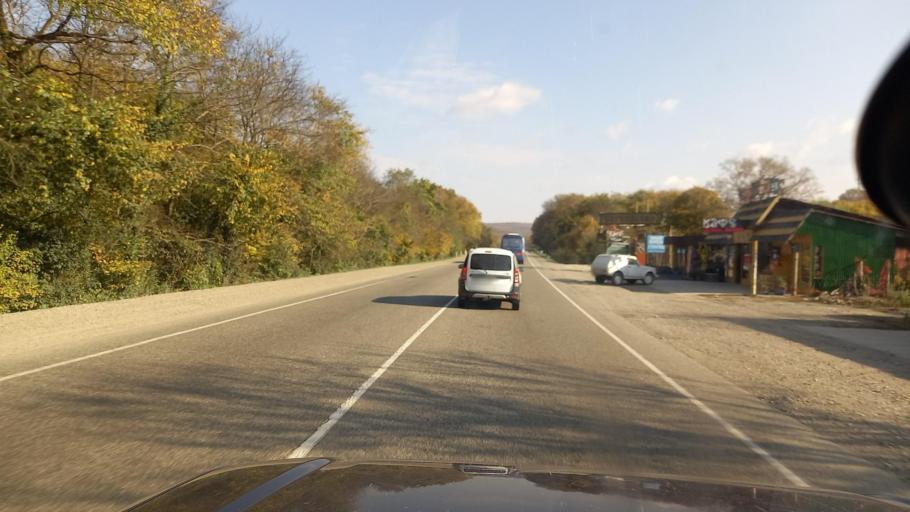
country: RU
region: Krasnodarskiy
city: Verkhnebakanskiy
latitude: 44.8559
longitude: 37.7316
